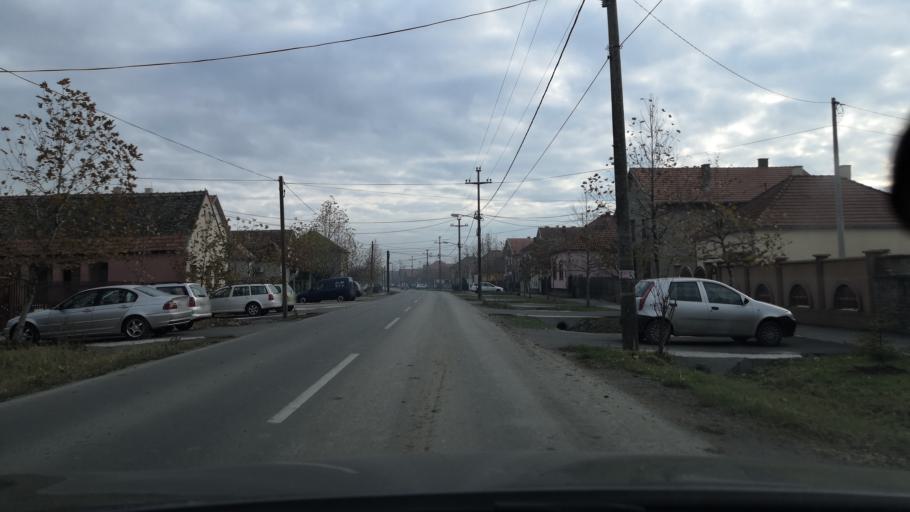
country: RS
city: Ugrinovci
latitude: 44.8725
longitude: 20.1960
